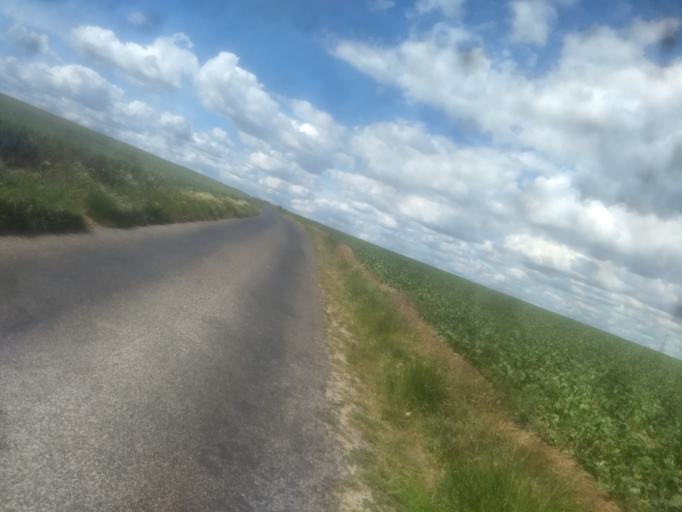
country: FR
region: Nord-Pas-de-Calais
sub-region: Departement du Pas-de-Calais
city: Tilloy-les-Mofflaines
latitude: 50.2619
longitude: 2.8191
